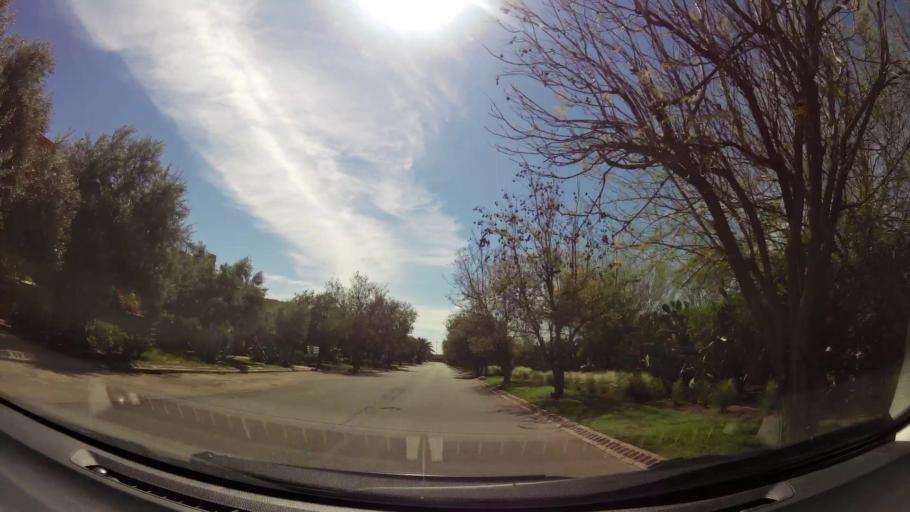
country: MA
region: Marrakech-Tensift-Al Haouz
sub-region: Marrakech
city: Marrakesh
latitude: 31.6180
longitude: -7.9471
